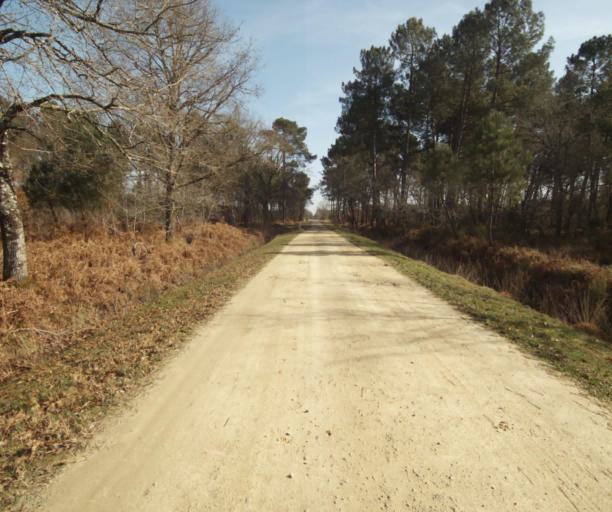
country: FR
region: Aquitaine
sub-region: Departement des Landes
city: Roquefort
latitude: 44.2197
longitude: -0.2225
